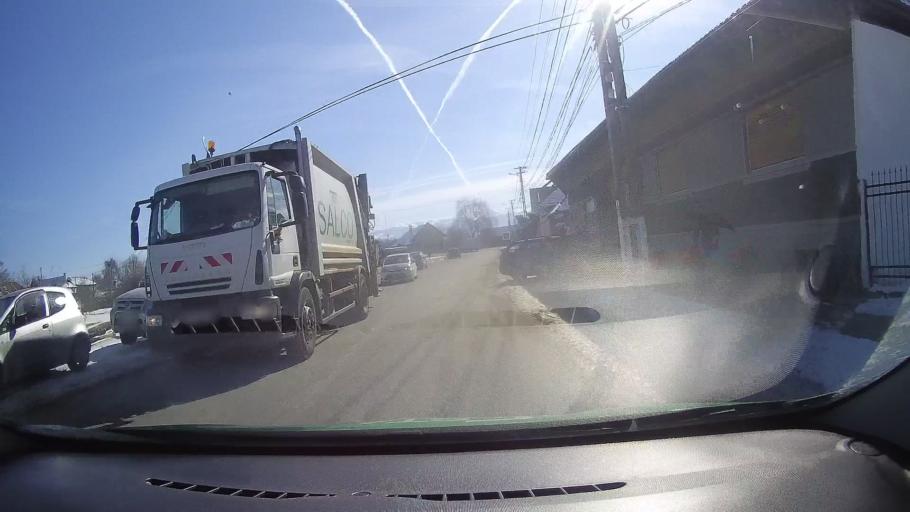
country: RO
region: Brasov
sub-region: Comuna Sambata de Sus
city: Sambata de Sus
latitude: 45.7600
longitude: 24.8245
